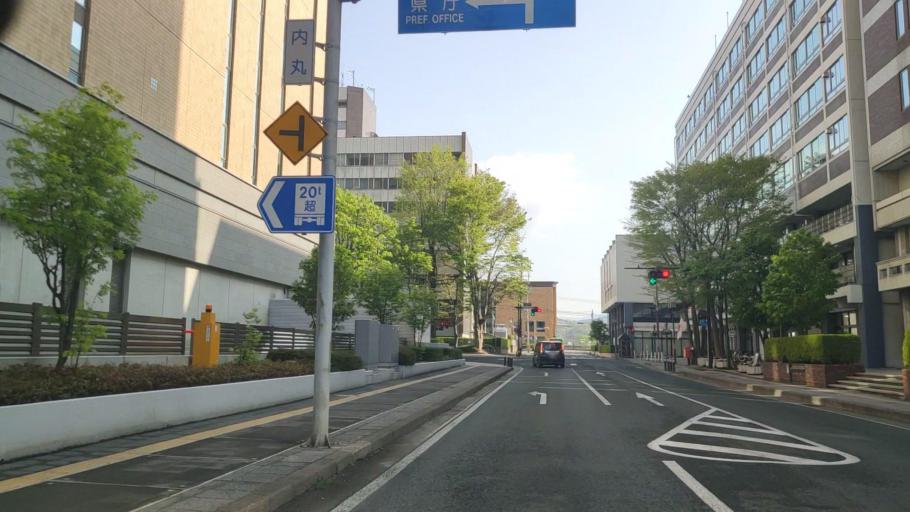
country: JP
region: Iwate
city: Morioka-shi
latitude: 39.7017
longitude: 141.1539
